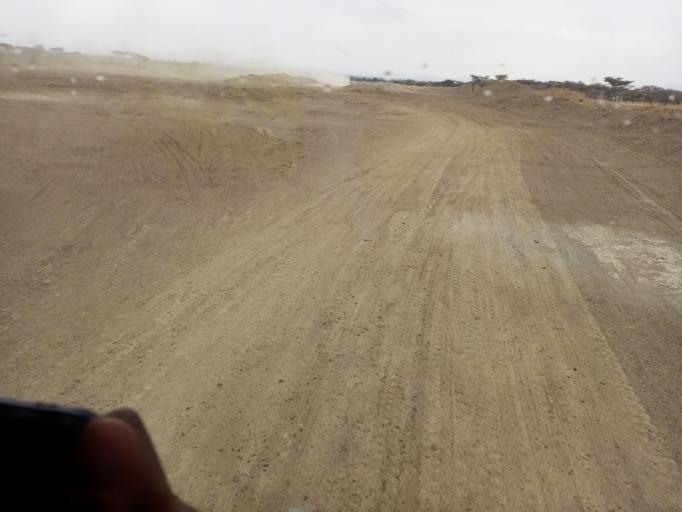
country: ET
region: Oromiya
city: Ziway
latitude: 7.7659
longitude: 38.6096
